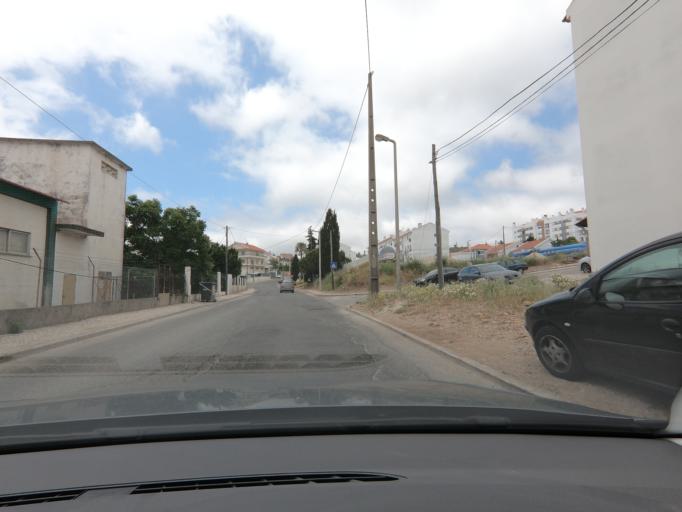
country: PT
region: Lisbon
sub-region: Oeiras
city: Porto Salvo
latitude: 38.7389
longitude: -9.3143
